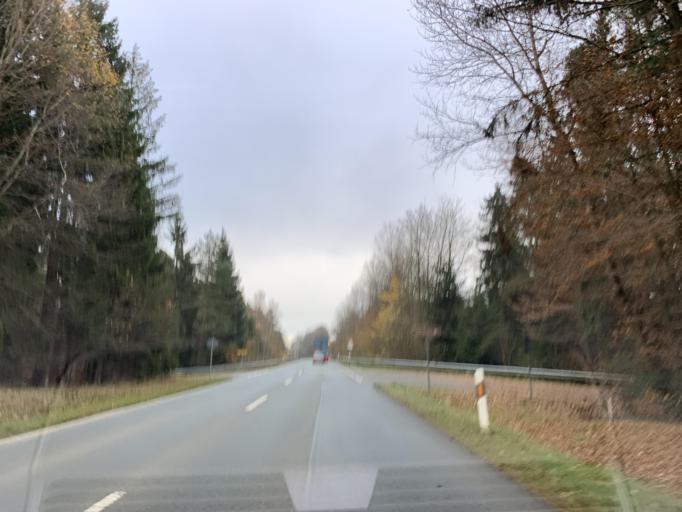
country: DE
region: Bavaria
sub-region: Upper Palatinate
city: Roetz
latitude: 49.3465
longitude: 12.4981
